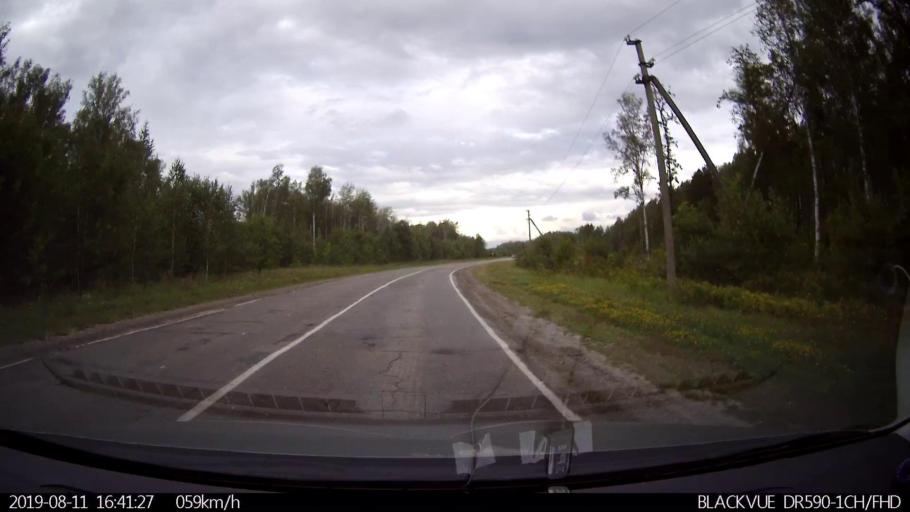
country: RU
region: Ulyanovsk
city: Mayna
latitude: 54.1535
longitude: 47.6529
